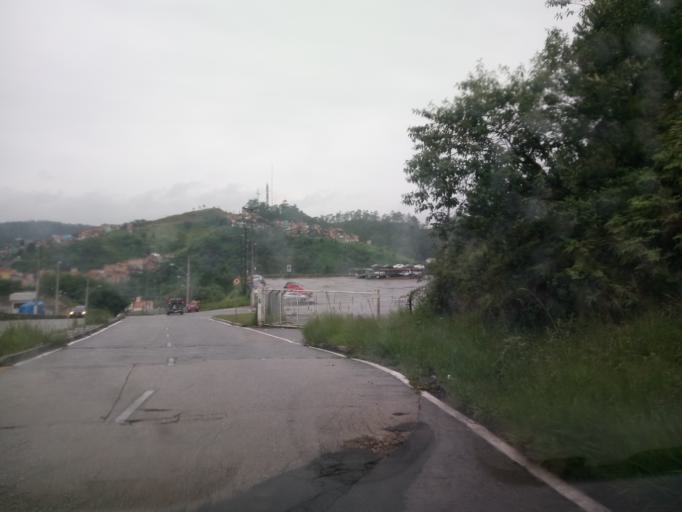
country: BR
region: Sao Paulo
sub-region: Sao Bernardo Do Campo
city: Sao Bernardo do Campo
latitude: -23.7455
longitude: -46.5432
